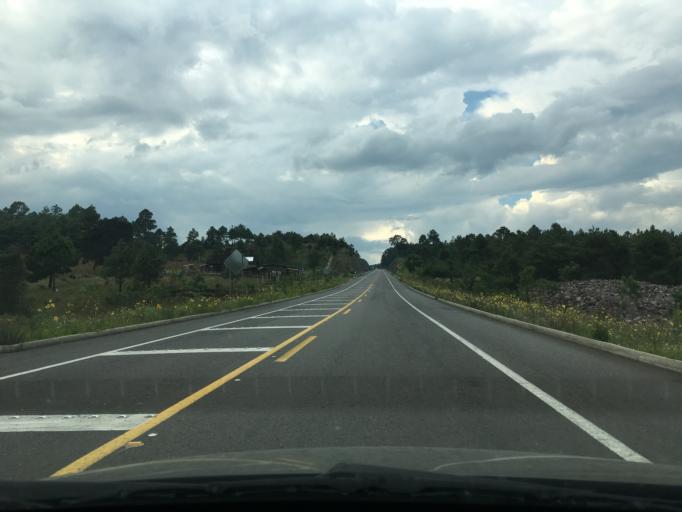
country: MX
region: Michoacan
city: Angahuan
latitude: 19.5129
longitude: -102.1674
